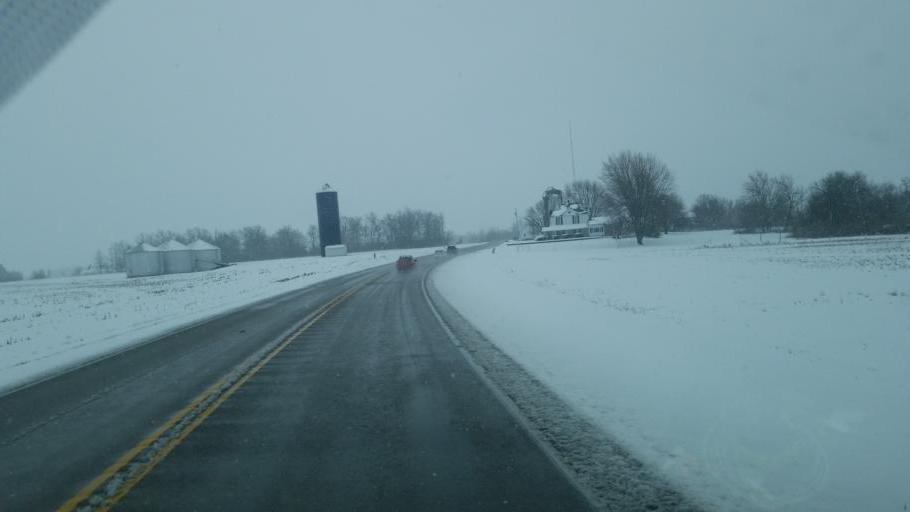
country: US
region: Indiana
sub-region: Randolph County
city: Parker City
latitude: 40.0816
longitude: -85.2752
